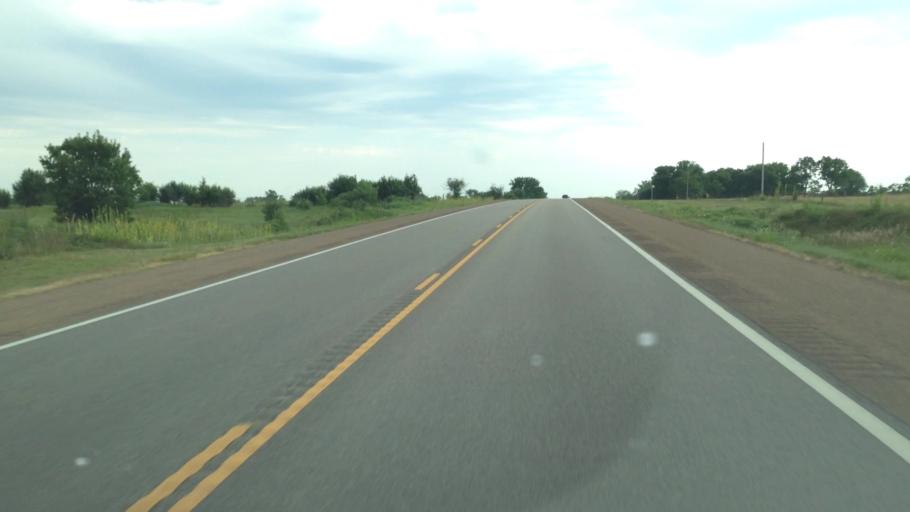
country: US
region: Kansas
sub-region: Woodson County
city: Yates Center
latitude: 38.0081
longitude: -95.7390
